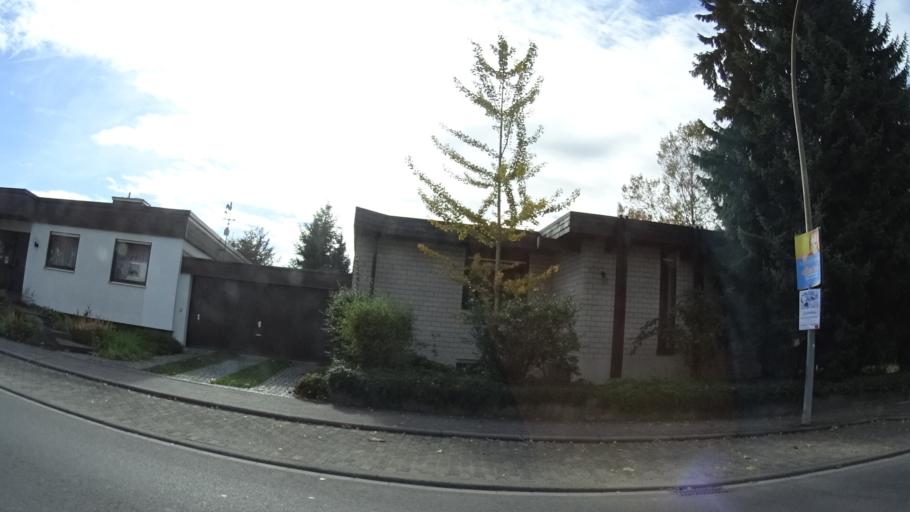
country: DE
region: Baden-Wuerttemberg
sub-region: Karlsruhe Region
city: Weingarten
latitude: 49.0489
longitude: 8.5215
